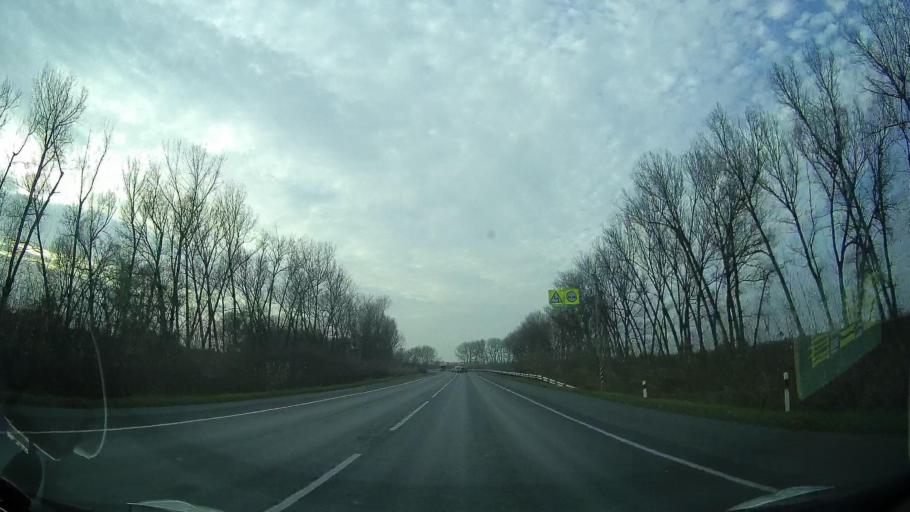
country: RU
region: Rostov
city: Starocherkasskaya
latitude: 47.1551
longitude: 40.1926
